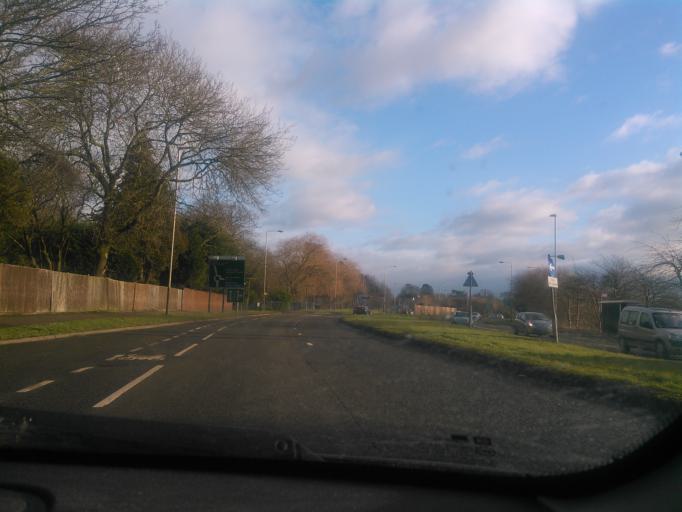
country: GB
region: England
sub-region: Leicestershire
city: Oadby
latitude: 52.6074
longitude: -1.0952
